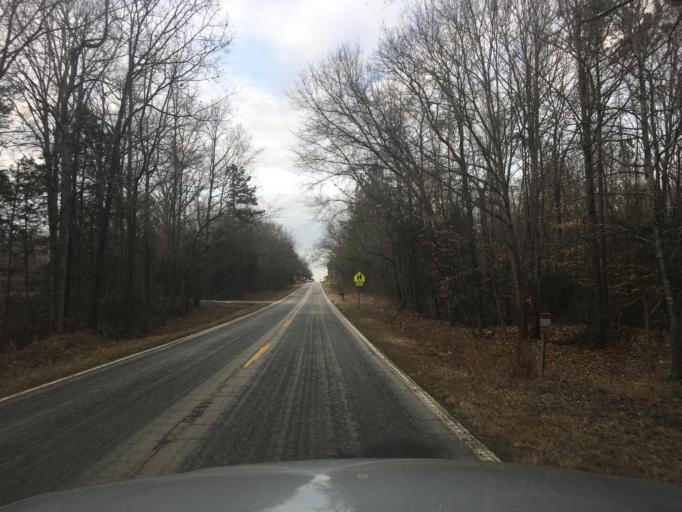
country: US
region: South Carolina
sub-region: Abbeville County
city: Due West
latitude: 34.2965
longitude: -82.4501
